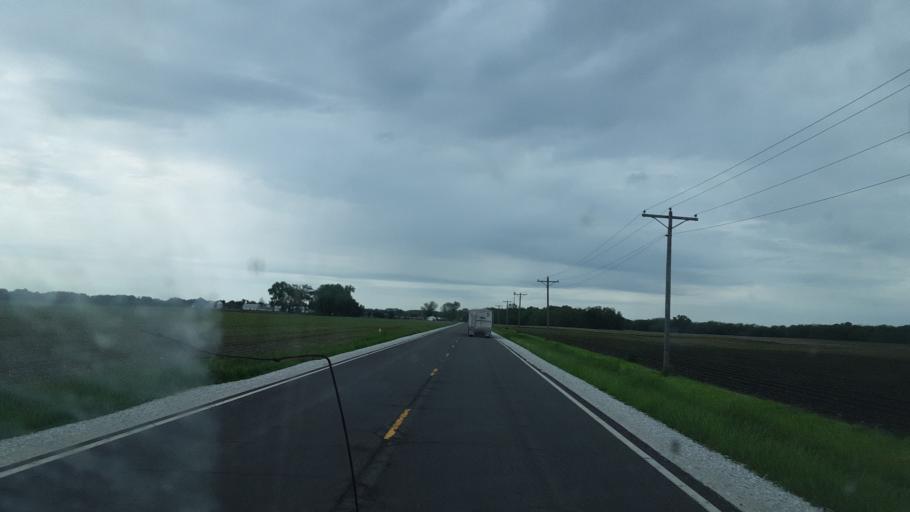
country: US
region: Illinois
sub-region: Fulton County
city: Lewistown
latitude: 40.3231
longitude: -90.1905
